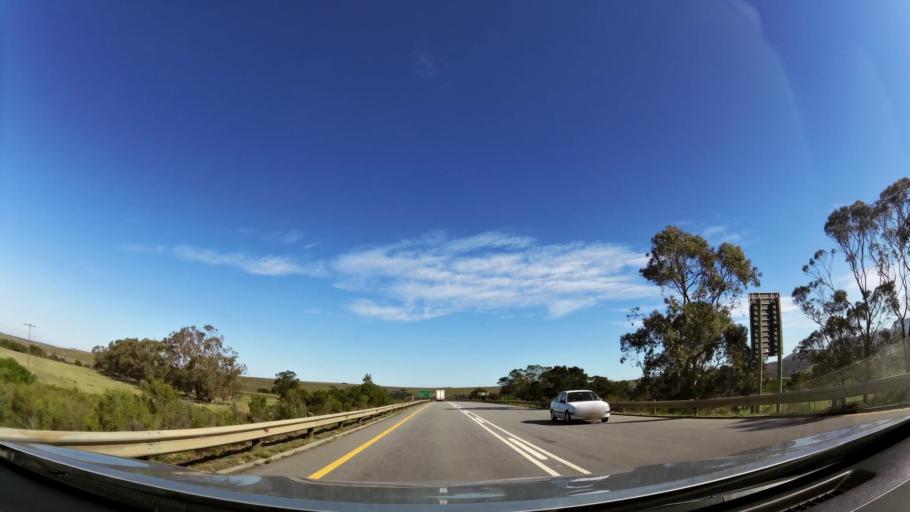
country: ZA
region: Eastern Cape
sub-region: Cacadu District Municipality
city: Kruisfontein
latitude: -34.0358
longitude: 24.5922
